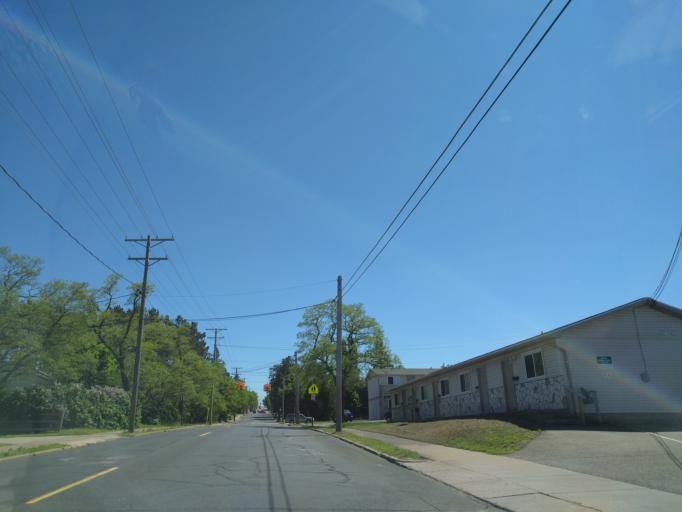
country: US
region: Michigan
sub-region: Marquette County
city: Marquette
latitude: 46.5576
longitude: -87.4121
